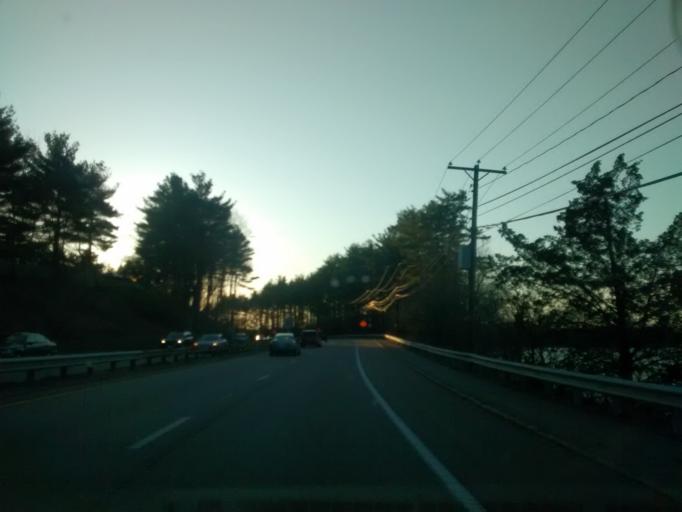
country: US
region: Massachusetts
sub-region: Middlesex County
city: Framingham Center
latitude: 42.2936
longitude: -71.4621
